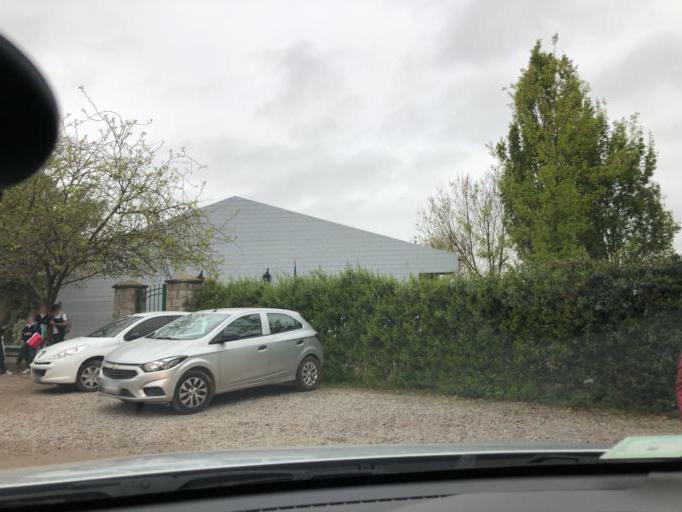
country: AR
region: Buenos Aires
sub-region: Partido de La Plata
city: La Plata
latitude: -34.9012
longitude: -58.0964
